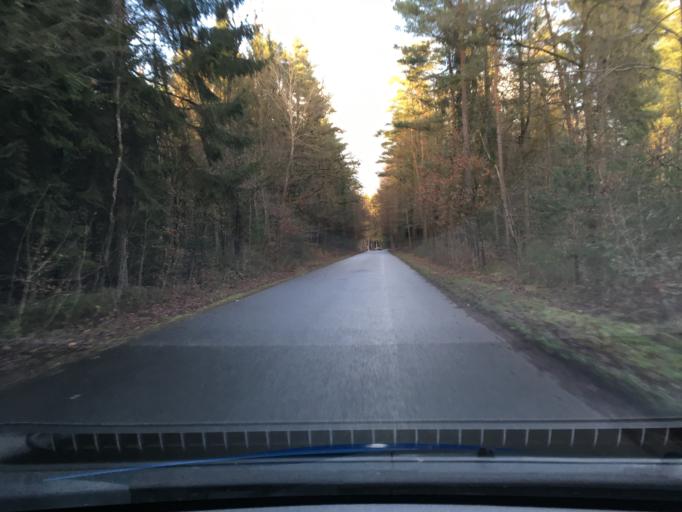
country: DE
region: Lower Saxony
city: Soderstorf
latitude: 53.0972
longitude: 10.1536
